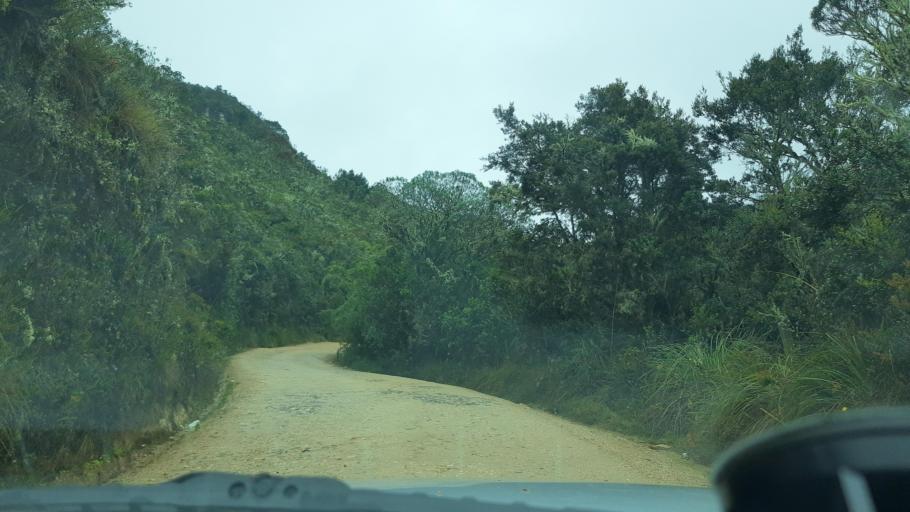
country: CO
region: Cundinamarca
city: Villapinzon
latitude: 5.2053
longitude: -73.5514
